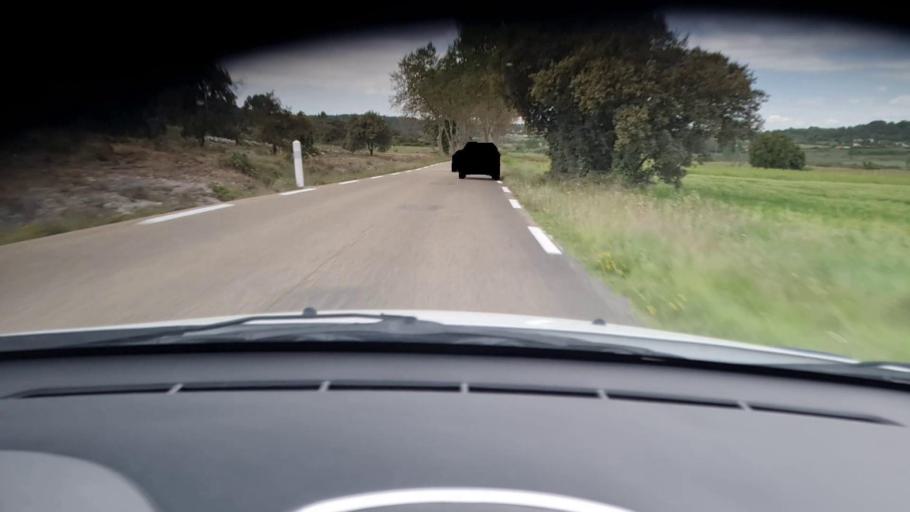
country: FR
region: Languedoc-Roussillon
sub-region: Departement du Gard
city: Blauzac
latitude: 43.9717
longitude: 4.3950
